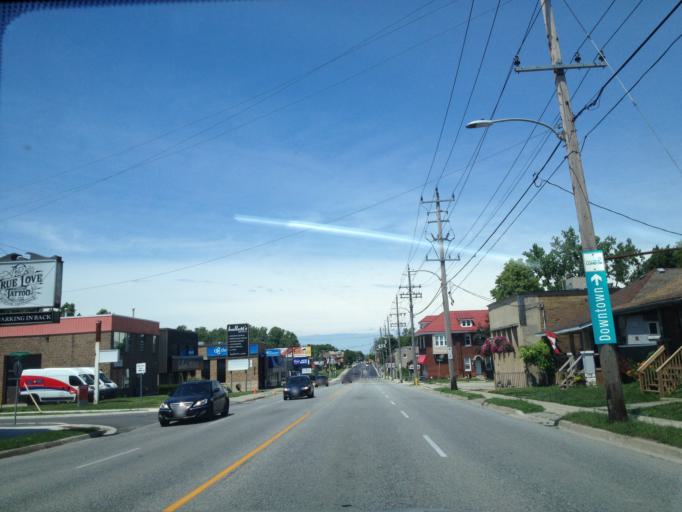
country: CA
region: Ontario
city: London
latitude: 42.9679
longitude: -81.2616
